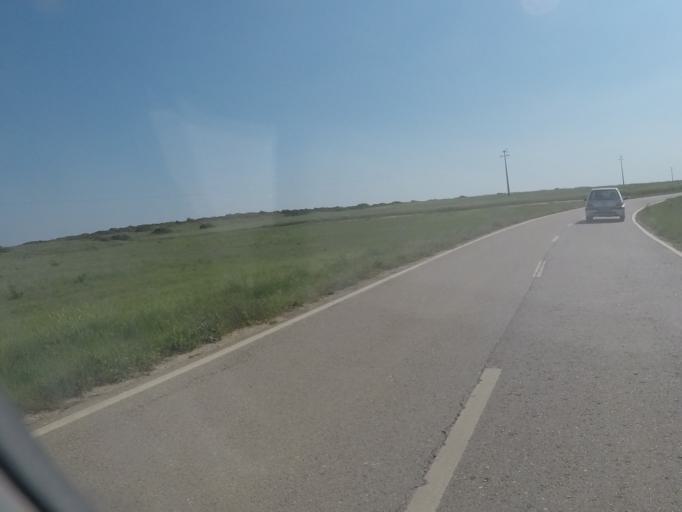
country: PT
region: Setubal
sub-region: Sesimbra
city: Sesimbra
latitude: 38.4198
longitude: -9.2029
